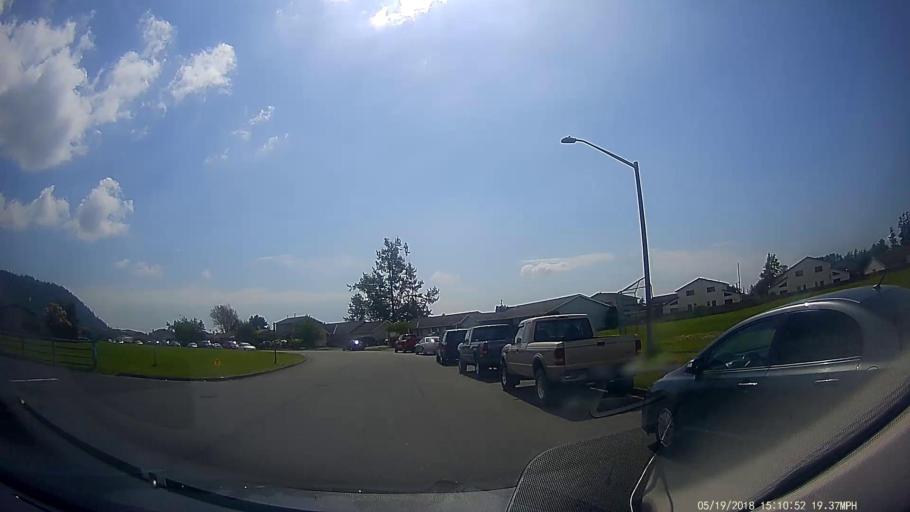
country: US
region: Washington
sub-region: Skagit County
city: Mount Vernon
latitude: 48.4165
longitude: -122.3107
